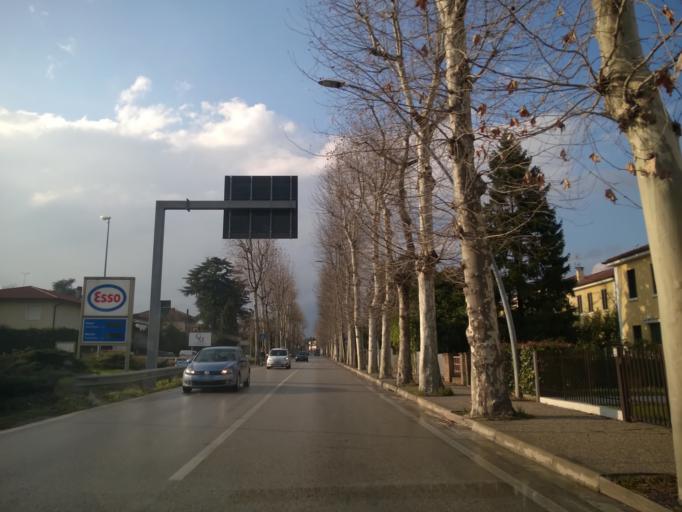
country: IT
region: Veneto
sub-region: Provincia di Vicenza
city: Thiene
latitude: 45.6974
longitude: 11.4816
